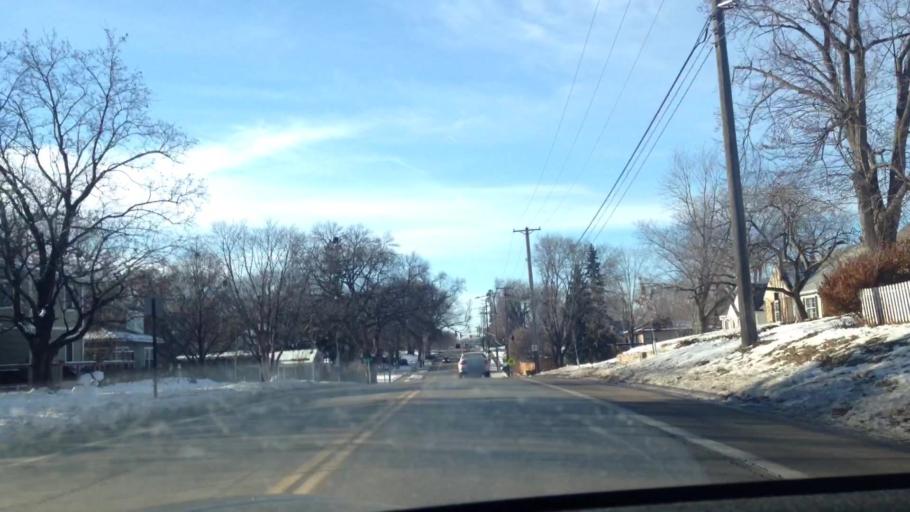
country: US
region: Minnesota
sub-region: Hennepin County
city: Saint Louis Park
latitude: 44.9495
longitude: -93.3761
